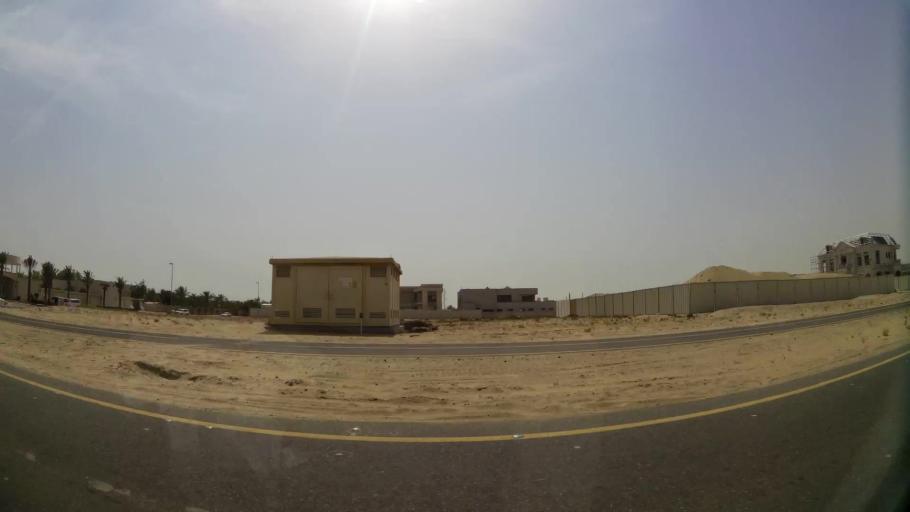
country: AE
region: Ash Shariqah
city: Sharjah
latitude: 25.2435
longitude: 55.4843
